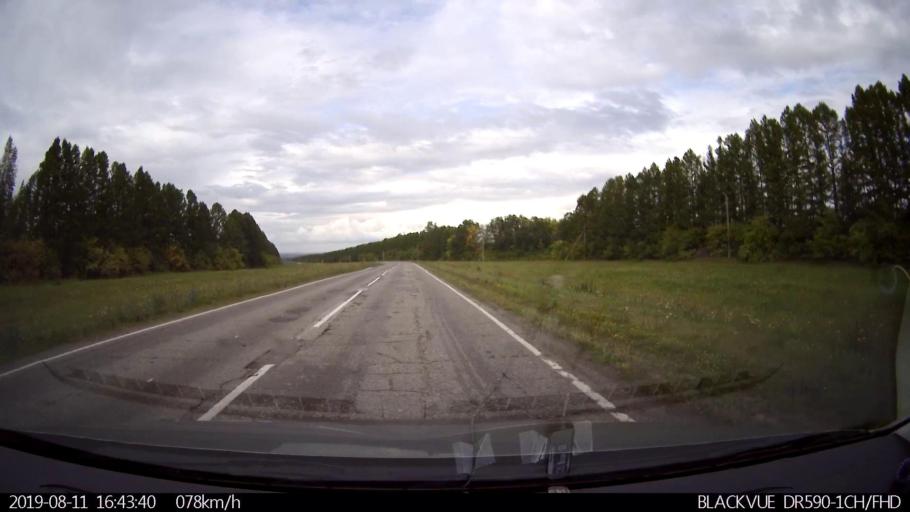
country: RU
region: Ulyanovsk
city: Mayna
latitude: 54.1711
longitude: 47.6745
